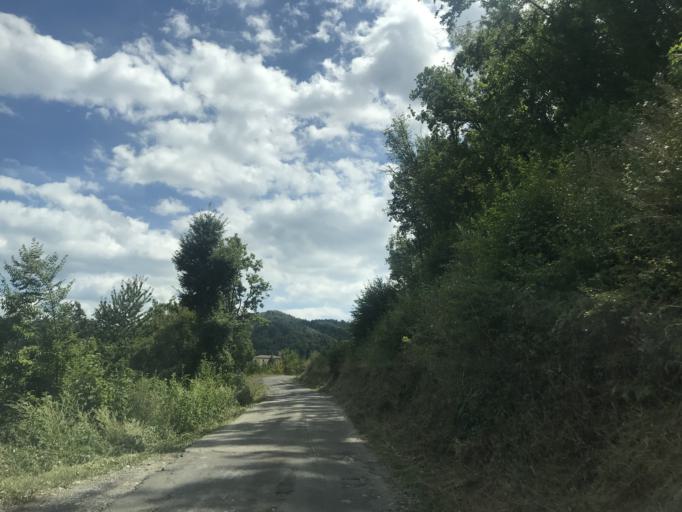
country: IT
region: Emilia-Romagna
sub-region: Provincia di Bologna
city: Grizzana Morandi
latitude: 44.2420
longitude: 11.1181
